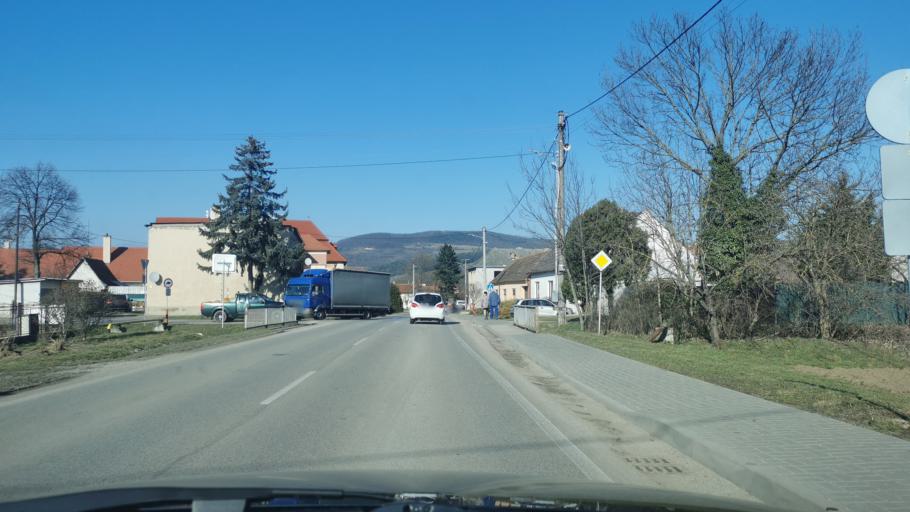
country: SK
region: Trnavsky
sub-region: Okres Senica
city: Senica
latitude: 48.7298
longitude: 17.4038
